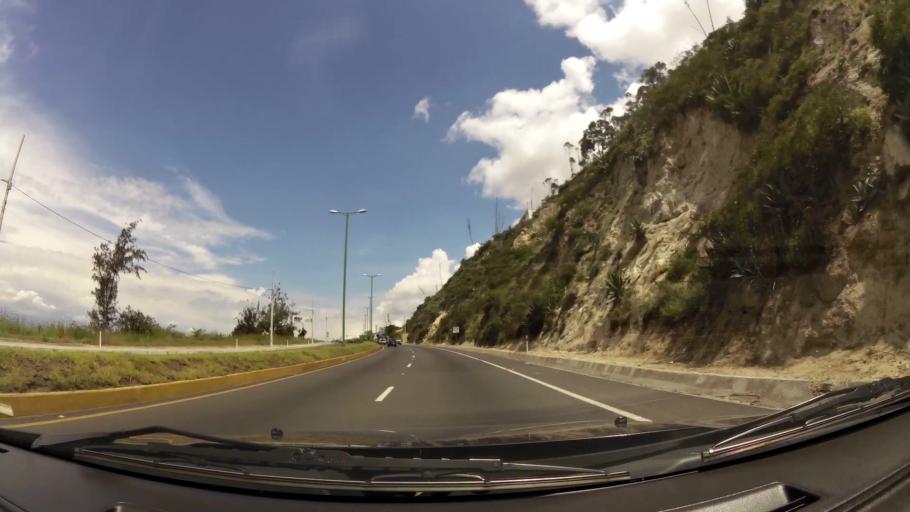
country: EC
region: Pichincha
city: Quito
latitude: -0.0948
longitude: -78.4172
